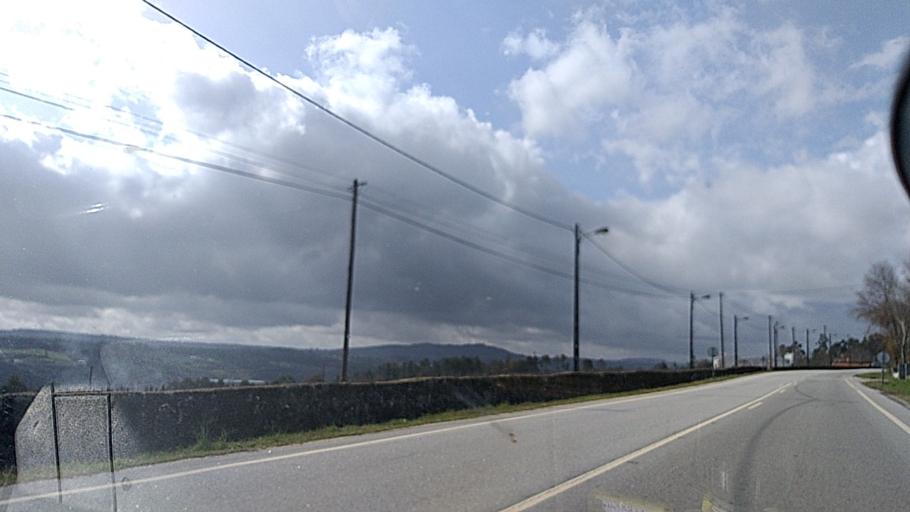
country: PT
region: Viseu
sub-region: Mangualde
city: Mangualde
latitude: 40.6616
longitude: -7.7181
